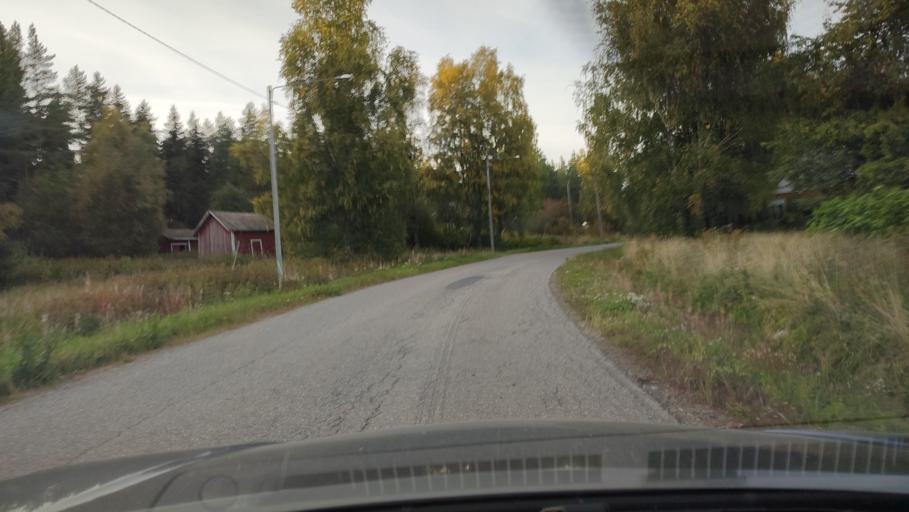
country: FI
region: Southern Ostrobothnia
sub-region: Suupohja
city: Karijoki
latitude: 62.1350
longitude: 21.5741
